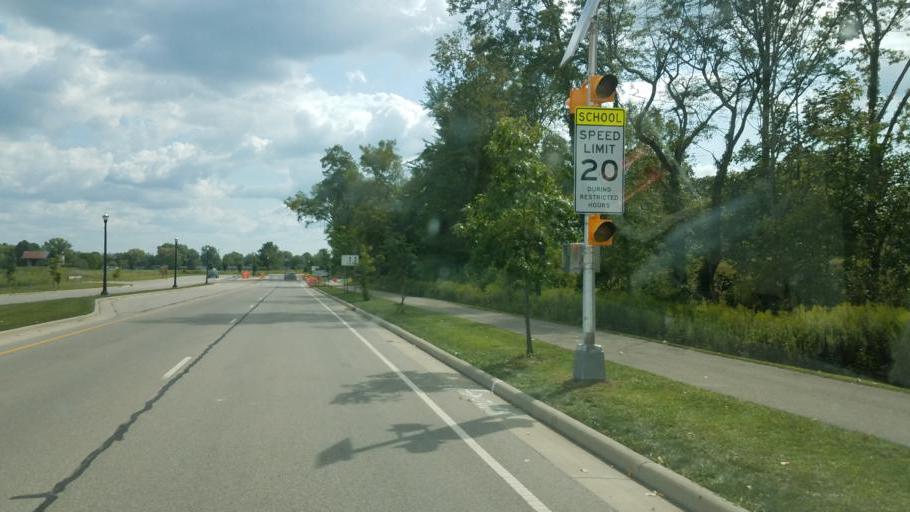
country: US
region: Ohio
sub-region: Delaware County
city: Lewis Center
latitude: 40.2331
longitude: -83.0355
